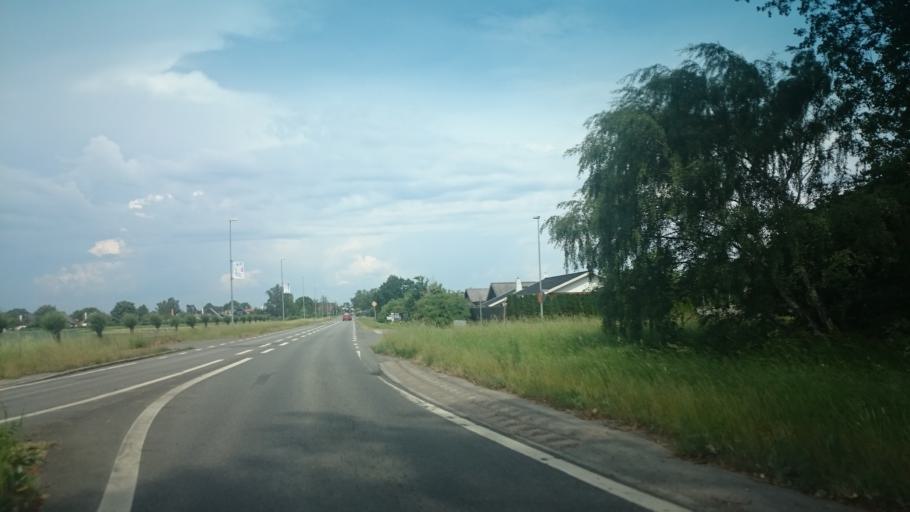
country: SE
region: Skane
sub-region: Kristianstads Kommun
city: Norra Asum
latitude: 56.0053
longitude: 14.1514
